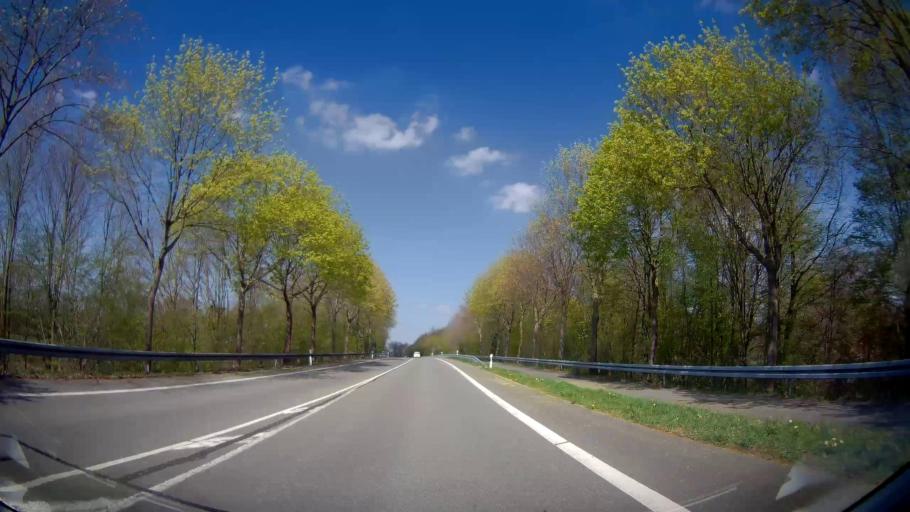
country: DE
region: North Rhine-Westphalia
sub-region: Regierungsbezirk Munster
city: Klein Reken
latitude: 51.7213
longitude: 7.0430
